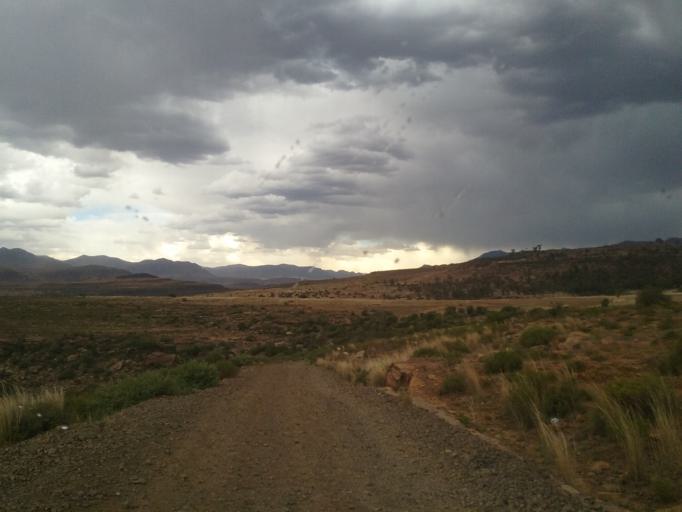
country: LS
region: Quthing
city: Quthing
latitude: -30.3043
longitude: 27.8128
